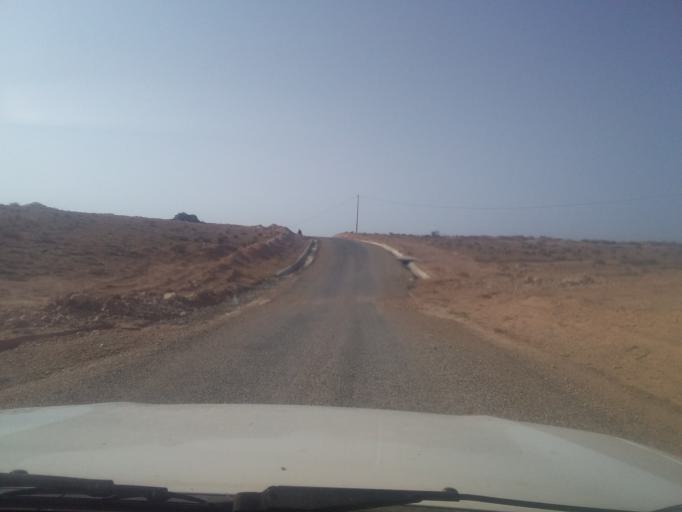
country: TN
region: Qabis
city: Matmata
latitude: 33.5820
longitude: 10.2613
